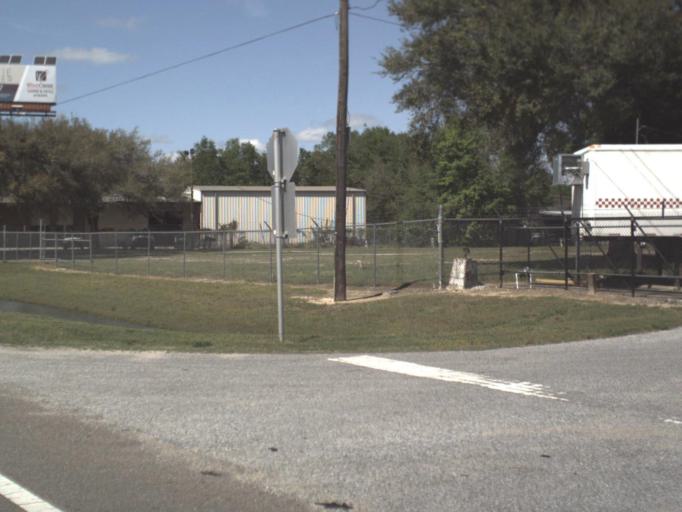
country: US
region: Florida
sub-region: Escambia County
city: Ensley
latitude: 30.5121
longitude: -87.2703
